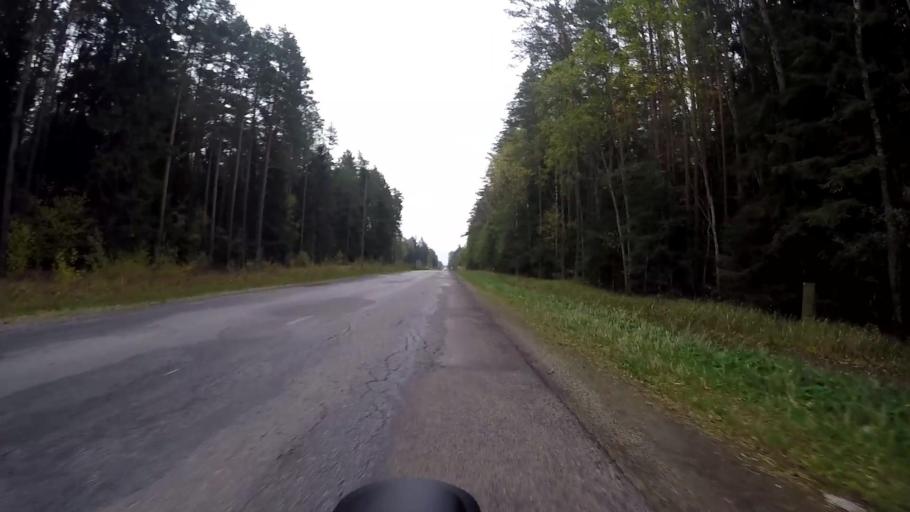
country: LV
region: Saulkrastu
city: Saulkrasti
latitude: 57.2714
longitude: 24.4843
